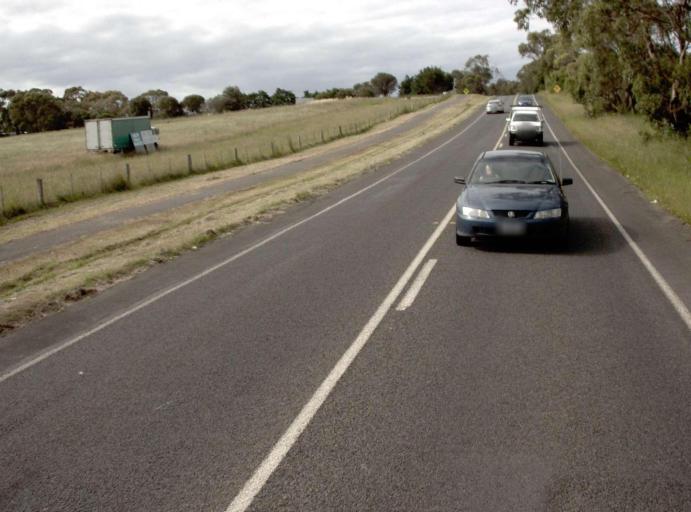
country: AU
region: Victoria
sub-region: Bass Coast
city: Phillip Island
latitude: -38.4765
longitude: 145.2390
